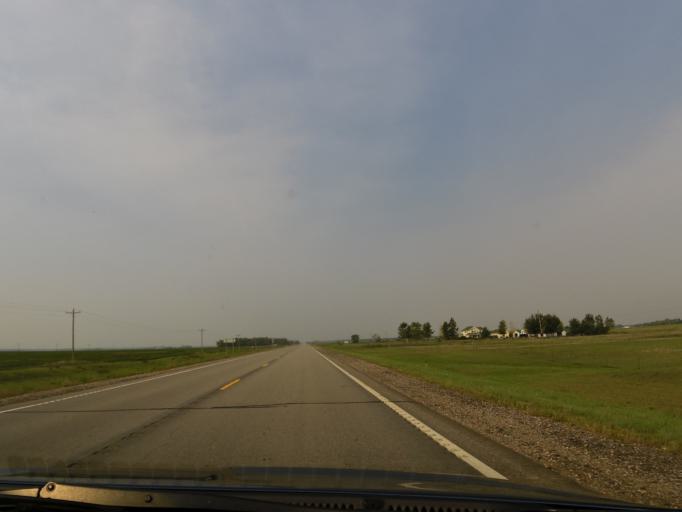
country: US
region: North Dakota
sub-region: Cass County
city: Horace
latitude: 46.6303
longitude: -96.8874
